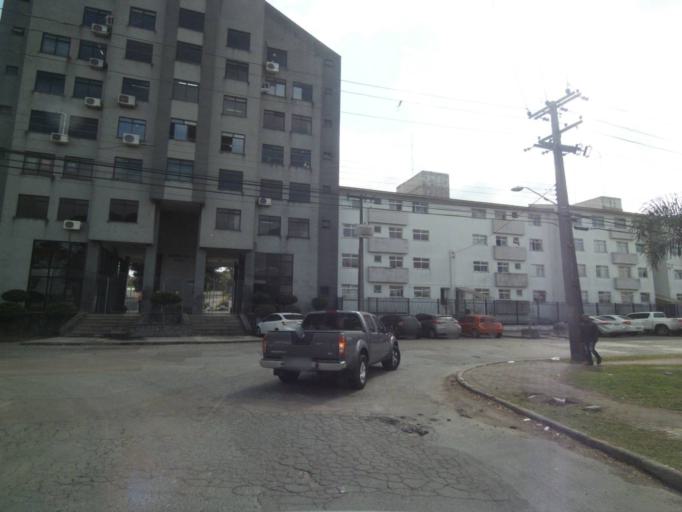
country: BR
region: Parana
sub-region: Curitiba
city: Curitiba
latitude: -25.4683
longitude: -49.2580
